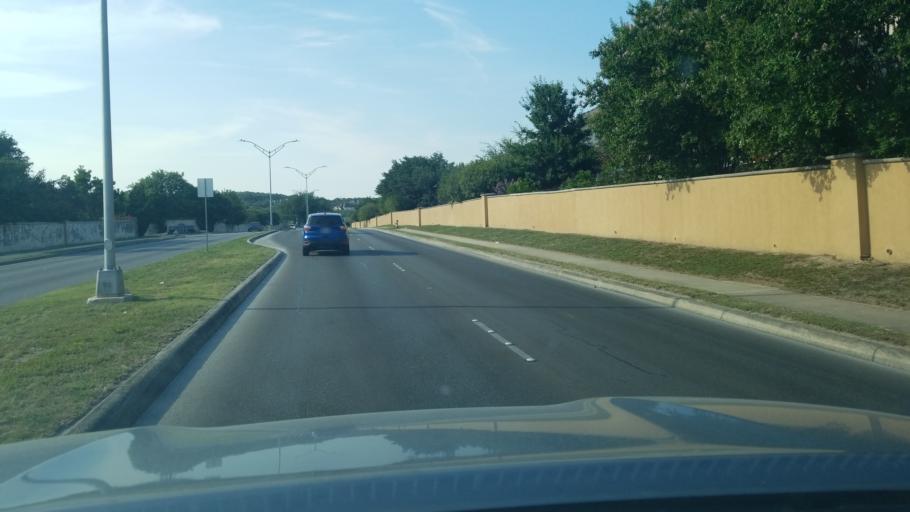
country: US
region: Texas
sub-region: Bexar County
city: Hollywood Park
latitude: 29.6498
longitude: -98.5033
